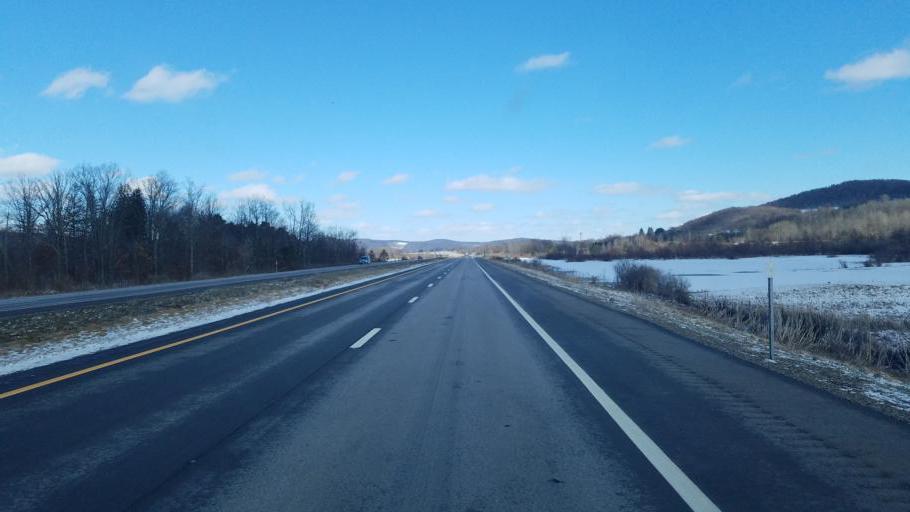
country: US
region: New York
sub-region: Cattaraugus County
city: Allegany
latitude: 42.0897
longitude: -78.5628
